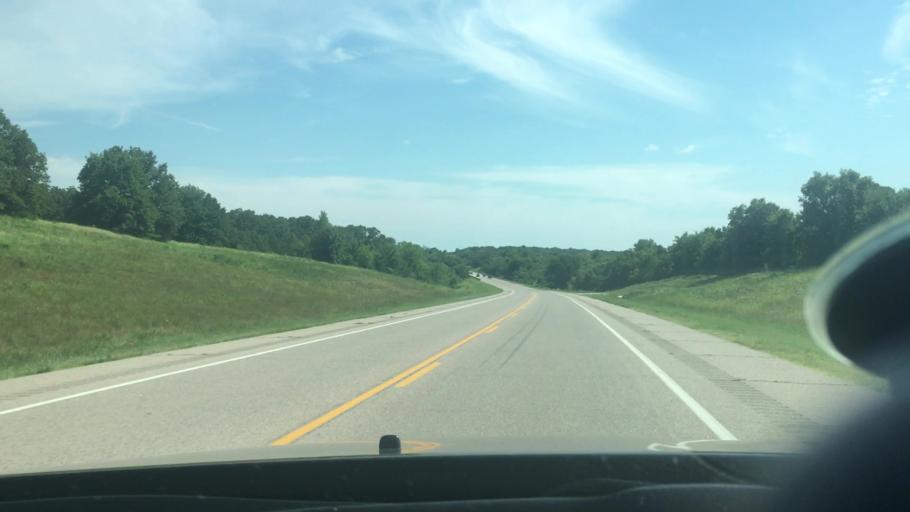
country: US
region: Oklahoma
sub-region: Seminole County
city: Seminole
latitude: 35.1344
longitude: -96.6784
